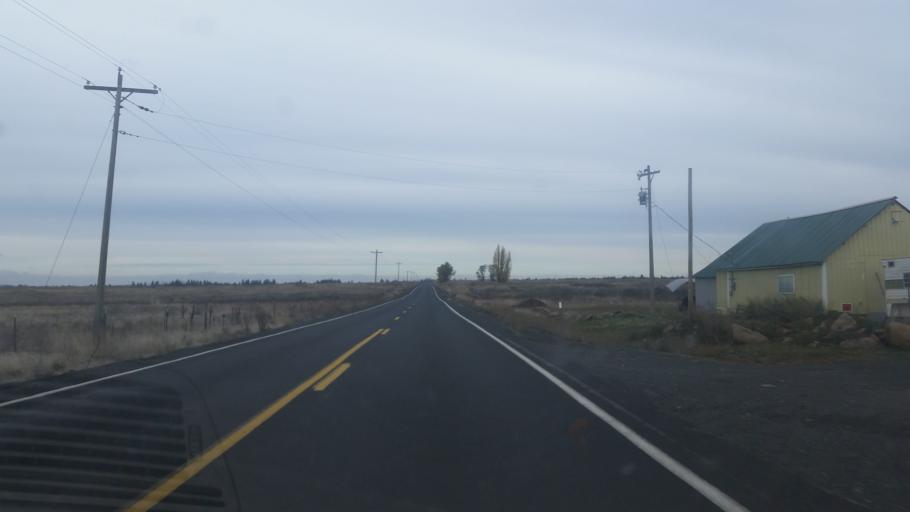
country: US
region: Washington
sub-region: Spokane County
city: Cheney
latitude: 47.4036
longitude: -117.4884
